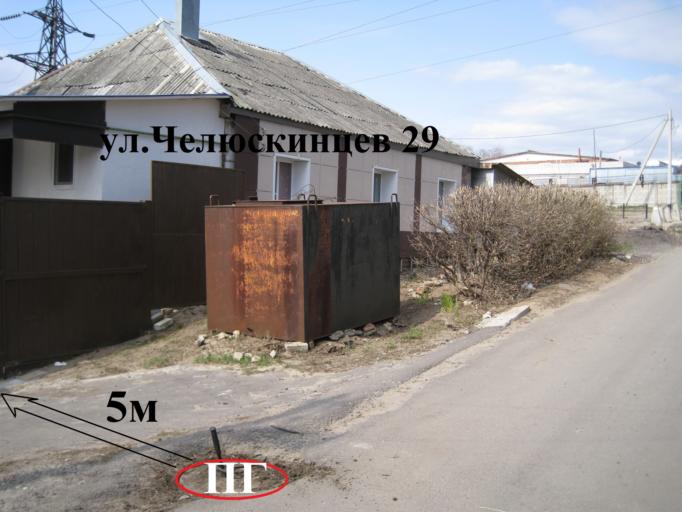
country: RU
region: Voronezj
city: Voronezh
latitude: 51.6413
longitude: 39.2017
